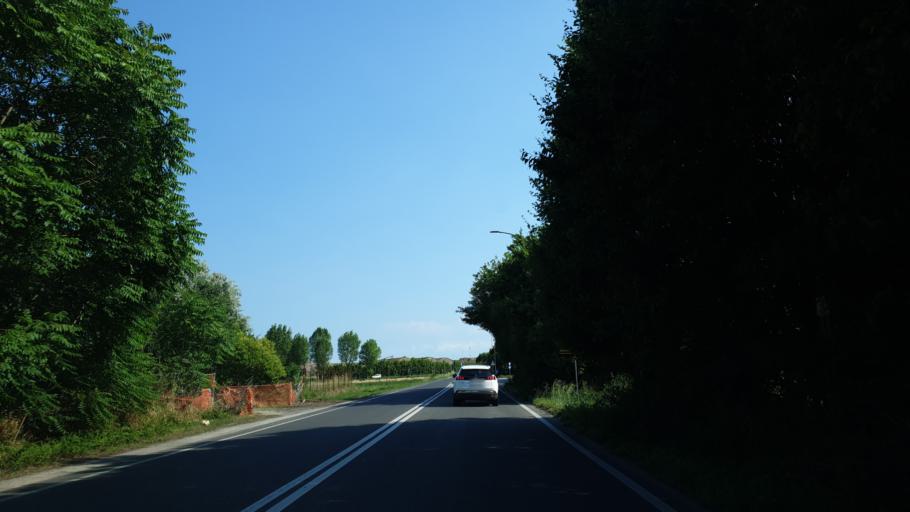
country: IT
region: Emilia-Romagna
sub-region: Provincia di Ravenna
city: Ravenna
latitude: 44.4298
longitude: 12.2147
